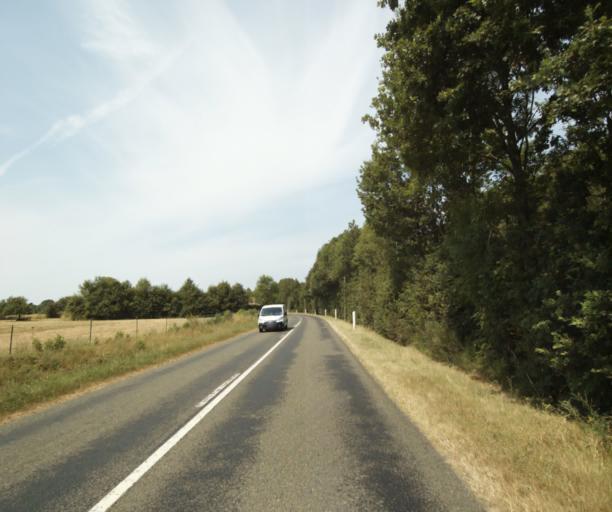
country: FR
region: Centre
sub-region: Departement d'Eure-et-Loir
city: Unverre
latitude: 48.1945
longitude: 1.0754
